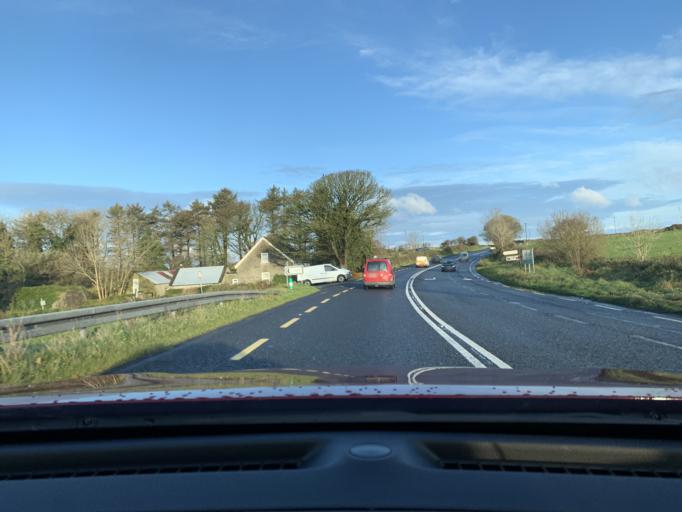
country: IE
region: Connaught
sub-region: Sligo
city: Sligo
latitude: 54.3623
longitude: -8.5263
